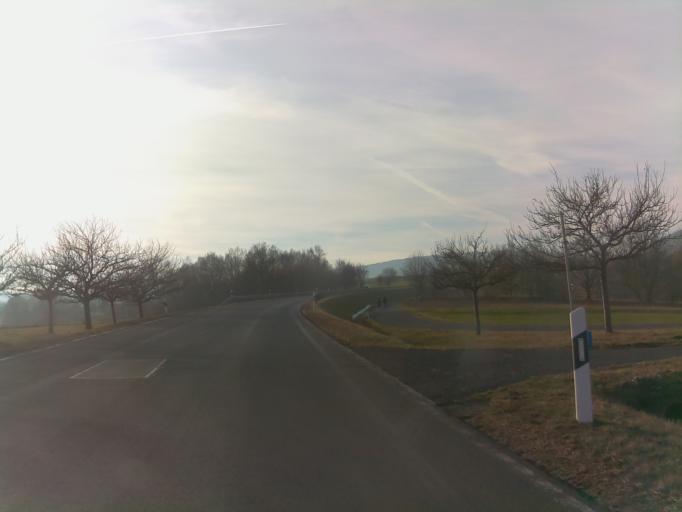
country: DE
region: Bavaria
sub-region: Regierungsbezirk Unterfranken
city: Sandberg
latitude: 50.3218
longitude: 9.9930
